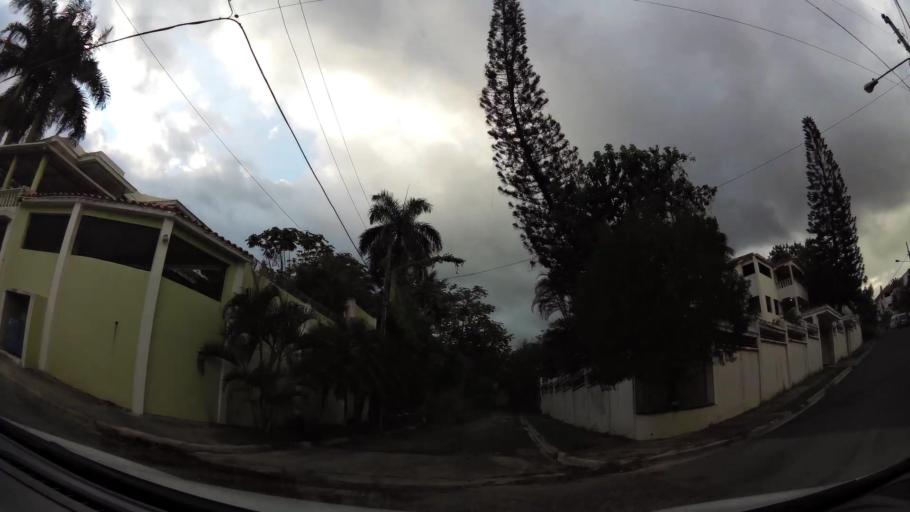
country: DO
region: Nacional
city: Santo Domingo
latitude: 18.4993
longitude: -69.9709
